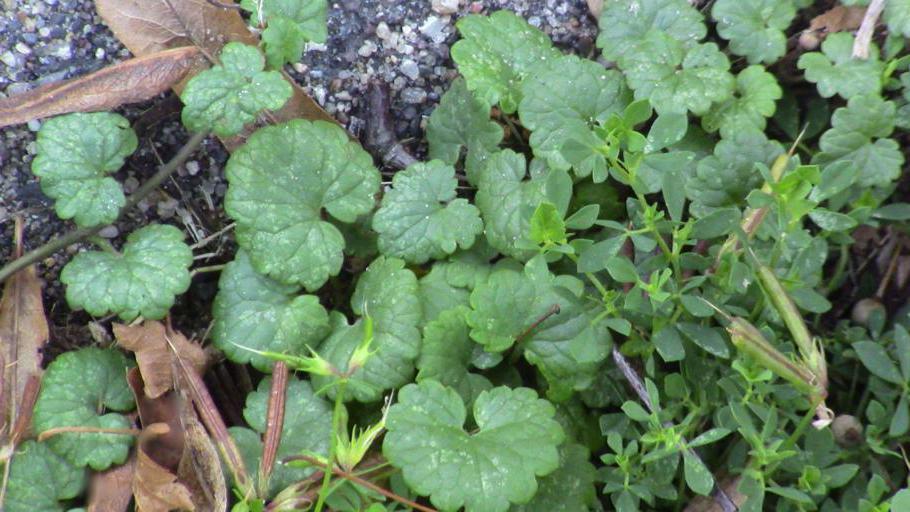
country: US
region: Minnesota
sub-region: Ramsey County
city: Saint Paul
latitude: 44.9334
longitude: -93.1001
